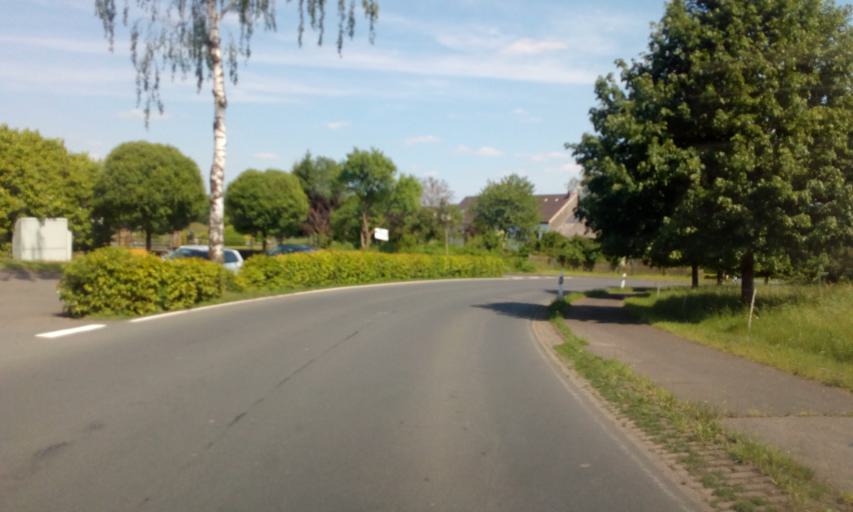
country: DE
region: Rheinland-Pfalz
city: Niedergeckler
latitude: 49.9699
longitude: 6.3049
